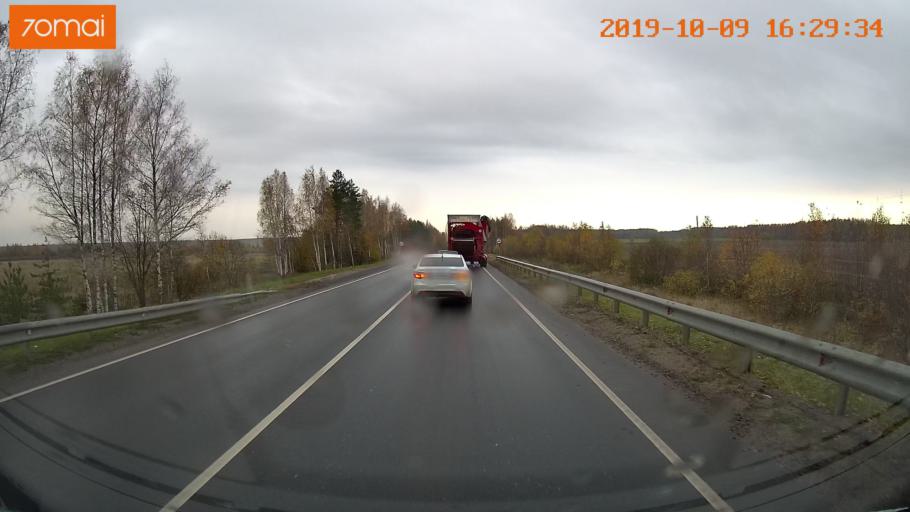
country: RU
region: Kostroma
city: Oktyabr'skiy
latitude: 57.6235
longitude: 40.9365
